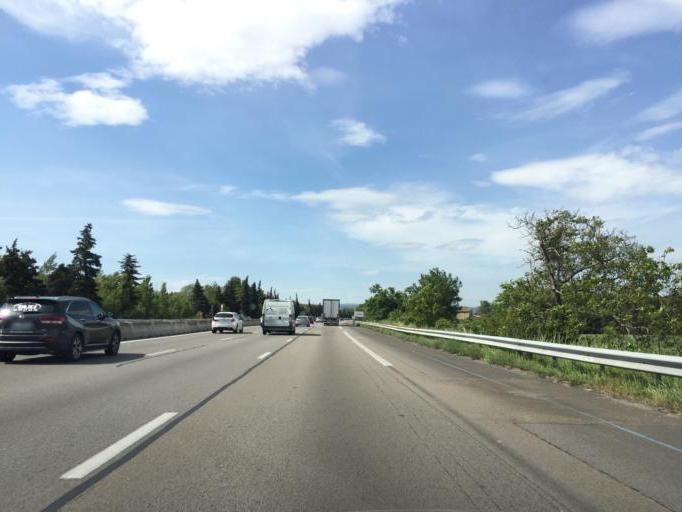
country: FR
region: Rhone-Alpes
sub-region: Departement de la Drome
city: Saulce-sur-Rhone
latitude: 44.6912
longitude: 4.7912
